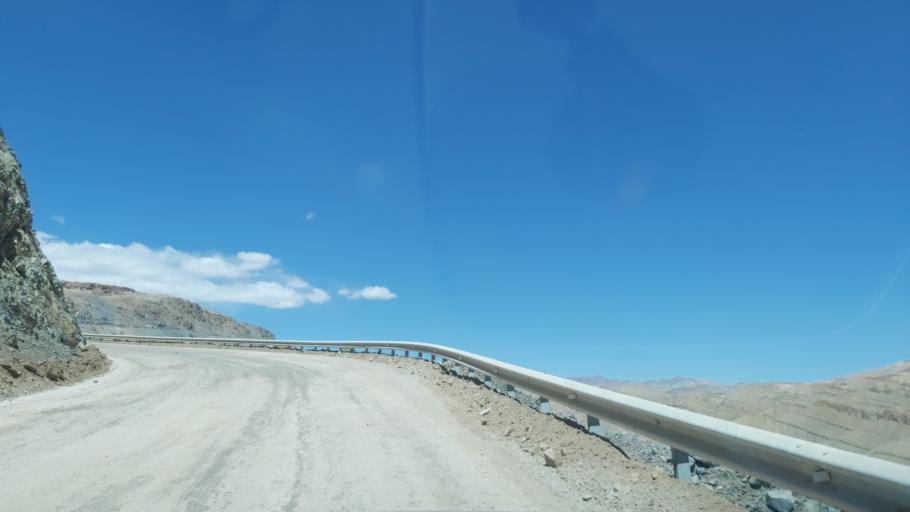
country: CL
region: Atacama
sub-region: Provincia de Chanaral
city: Diego de Almagro
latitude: -26.4580
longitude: -69.3116
